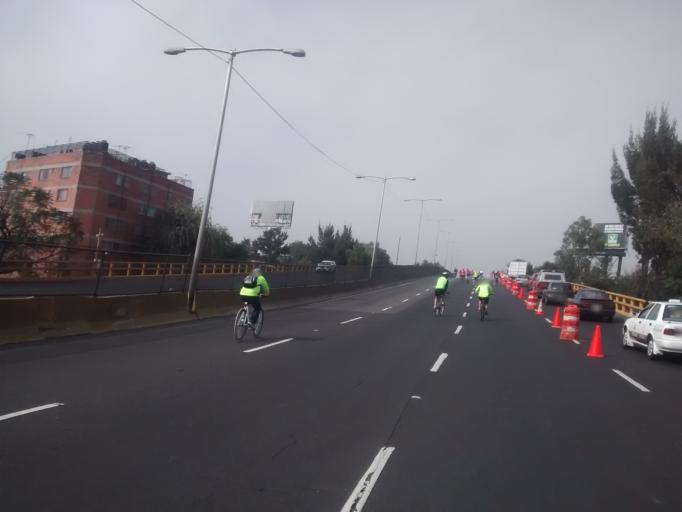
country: MX
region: Mexico City
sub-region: Iztacalco
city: Iztacalco
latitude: 19.3703
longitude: -99.1063
